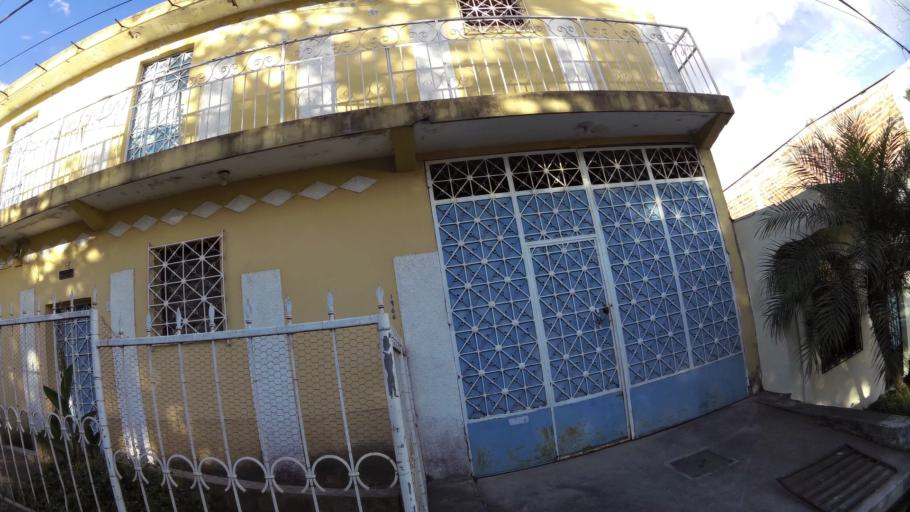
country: SV
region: Cuscatlan
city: Cojutepeque
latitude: 13.7126
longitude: -88.9294
